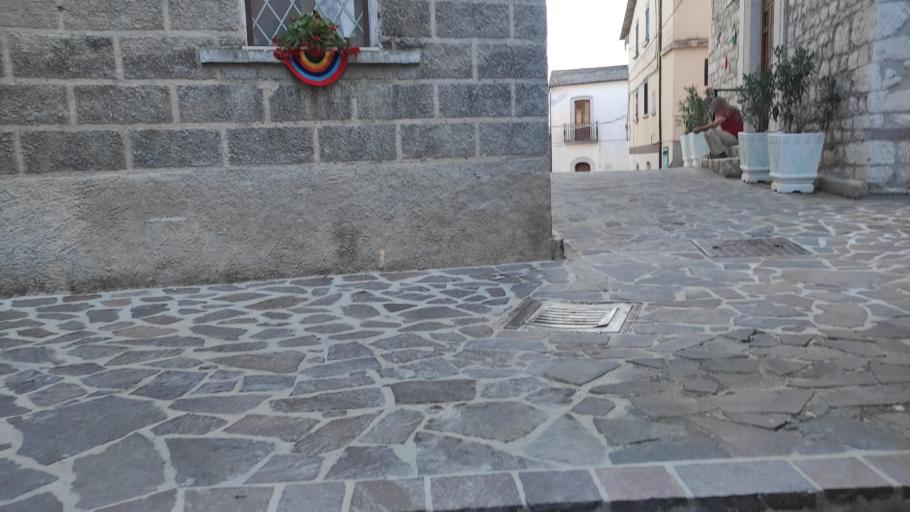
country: IT
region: Abruzzo
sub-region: Provincia di Chieti
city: Fallo
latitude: 41.9383
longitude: 14.3240
